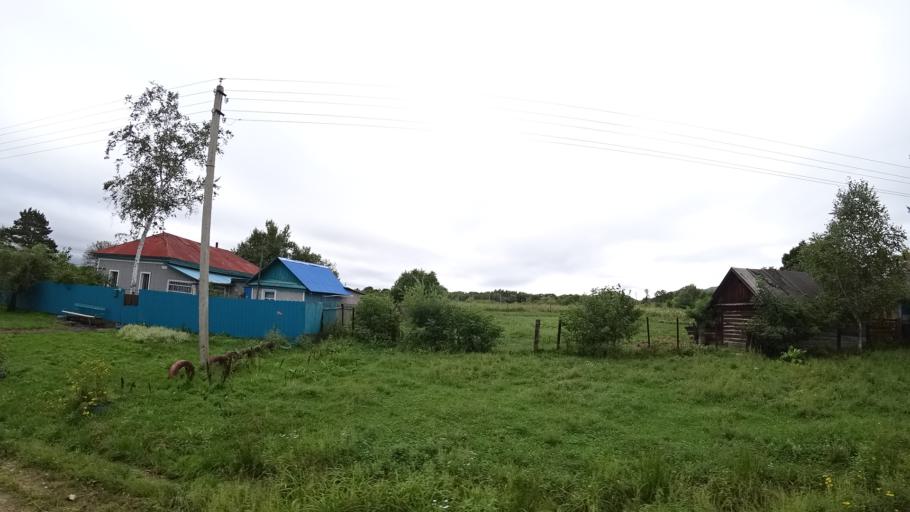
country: RU
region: Primorskiy
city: Rettikhovka
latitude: 44.1364
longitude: 132.6432
